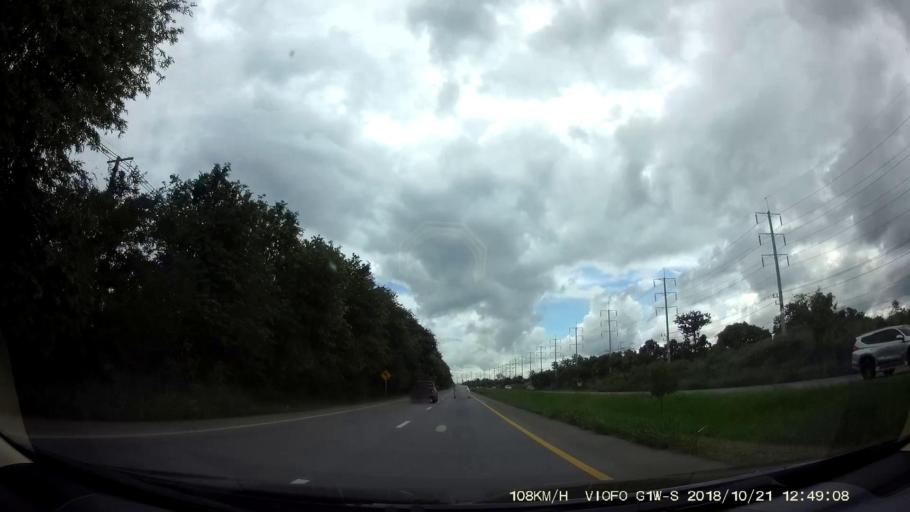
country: TH
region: Nakhon Ratchasima
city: Amphoe Sikhiu
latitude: 14.9013
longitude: 101.6841
